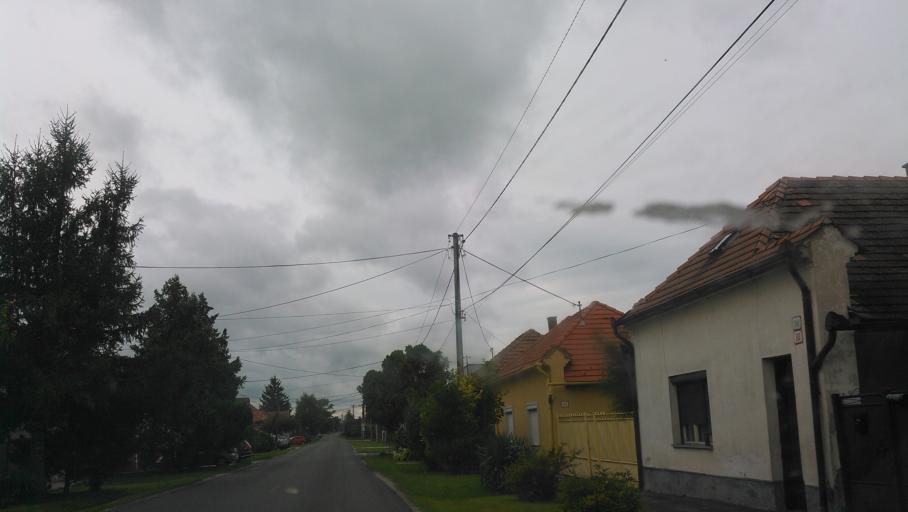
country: SK
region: Trnavsky
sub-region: Okres Dunajska Streda
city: Velky Meder
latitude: 47.8918
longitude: 17.8041
